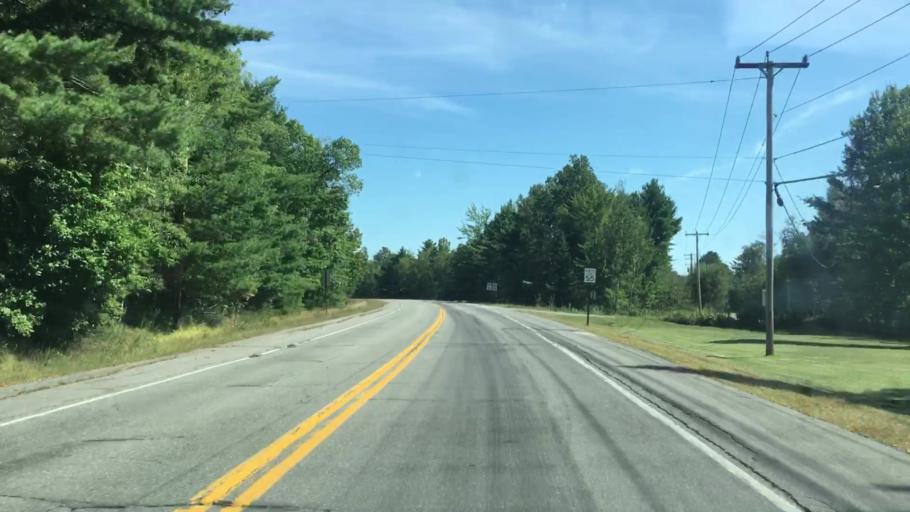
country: US
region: Maine
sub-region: Piscataquis County
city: Milo
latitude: 45.2300
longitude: -68.9528
